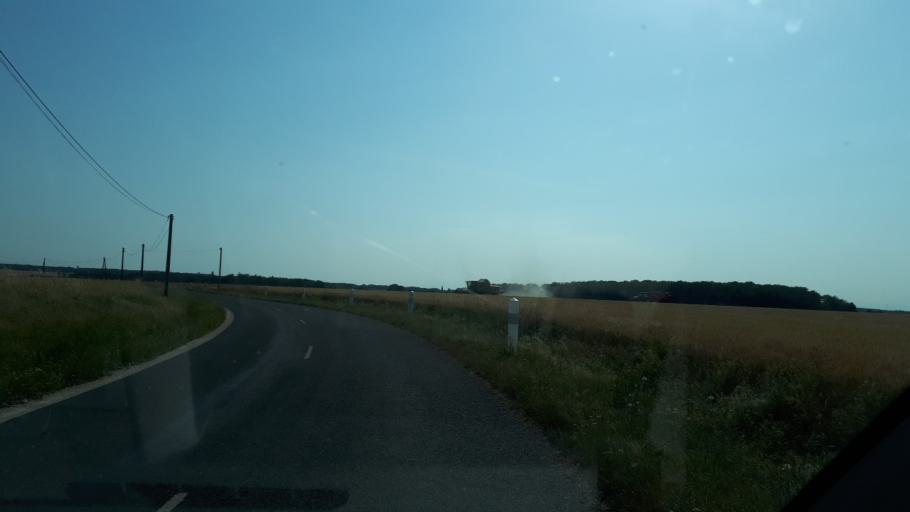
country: FR
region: Centre
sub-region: Departement du Loir-et-Cher
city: Droue
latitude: 48.0473
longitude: 1.0946
